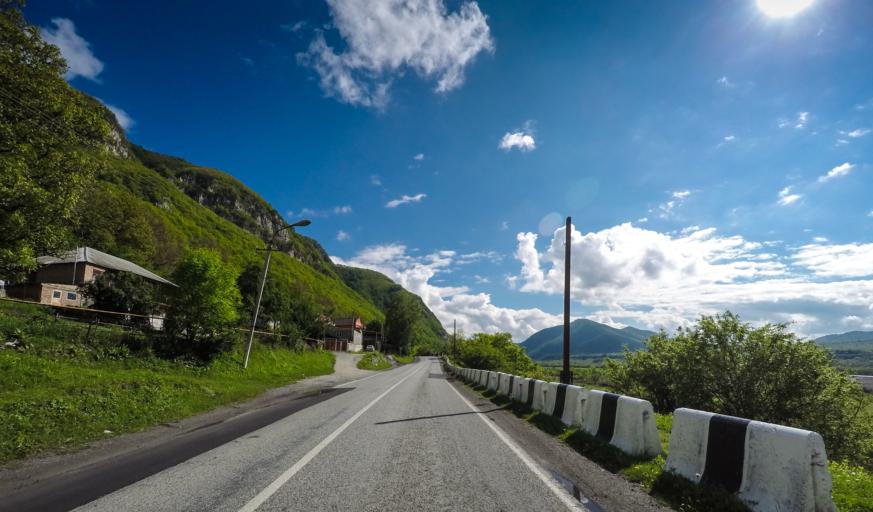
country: RU
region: North Ossetia
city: Vladikavkaz
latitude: 42.9323
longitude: 44.6392
